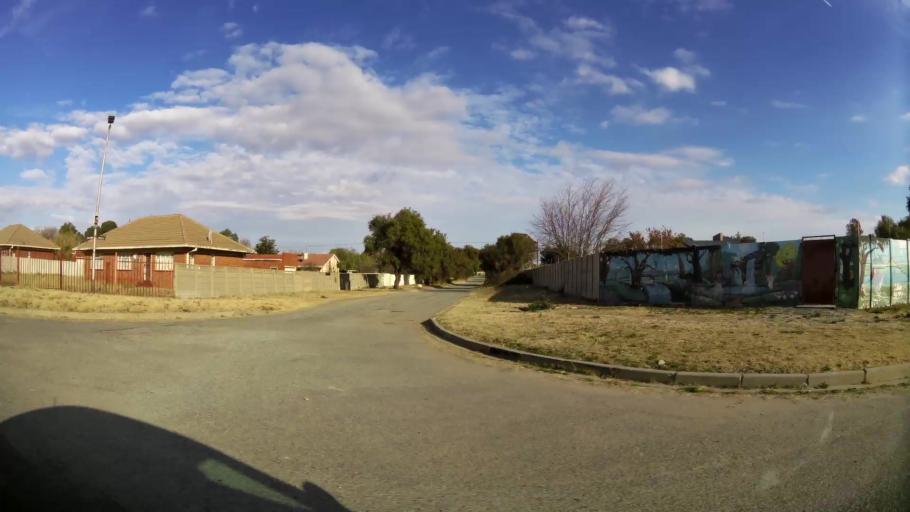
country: ZA
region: Orange Free State
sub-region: Lejweleputswa District Municipality
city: Welkom
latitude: -27.9873
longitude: 26.7064
